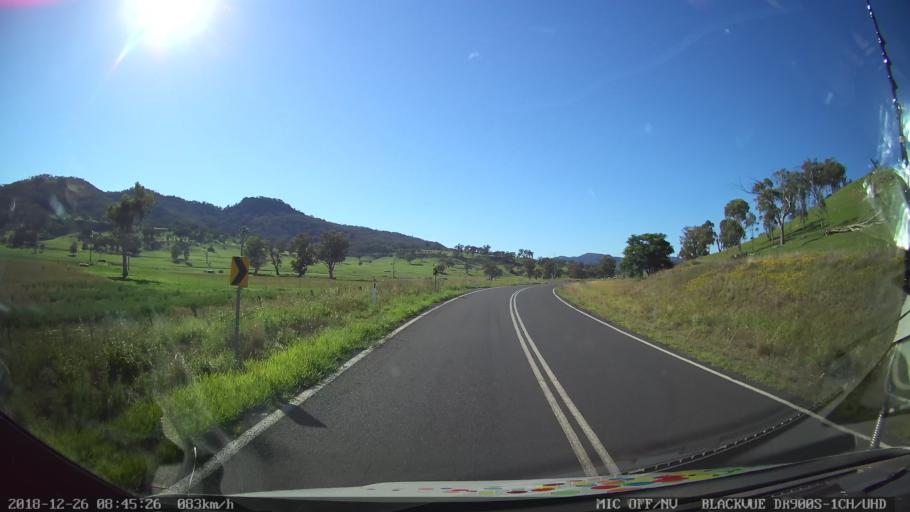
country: AU
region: New South Wales
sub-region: Mid-Western Regional
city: Kandos
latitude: -32.5251
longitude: 150.0868
